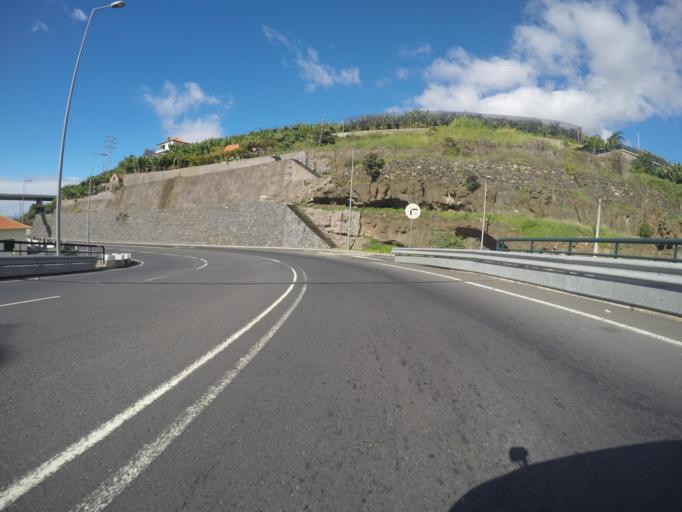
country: PT
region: Madeira
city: Camara de Lobos
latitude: 32.6530
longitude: -16.9593
